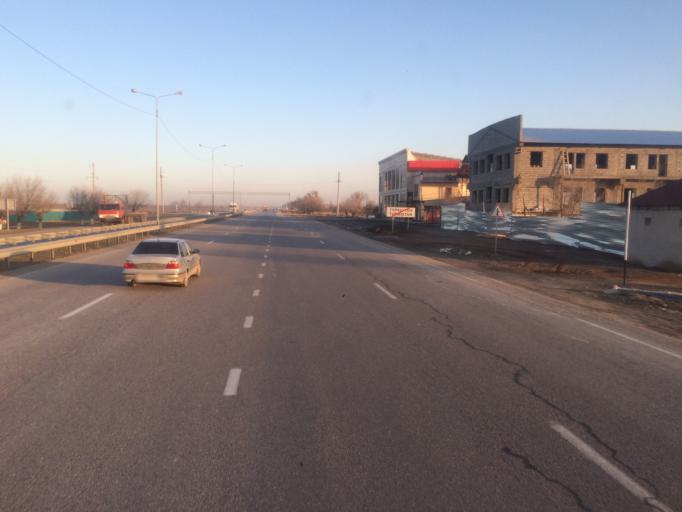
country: KZ
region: Ongtustik Qazaqstan
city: Turkestan
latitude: 43.2726
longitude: 68.3430
